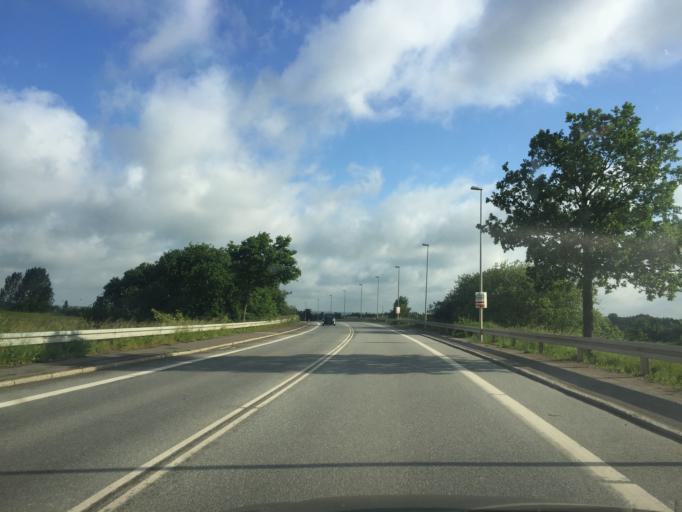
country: DK
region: Zealand
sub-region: Slagelse Kommune
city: Slagelse
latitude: 55.4110
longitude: 11.4023
